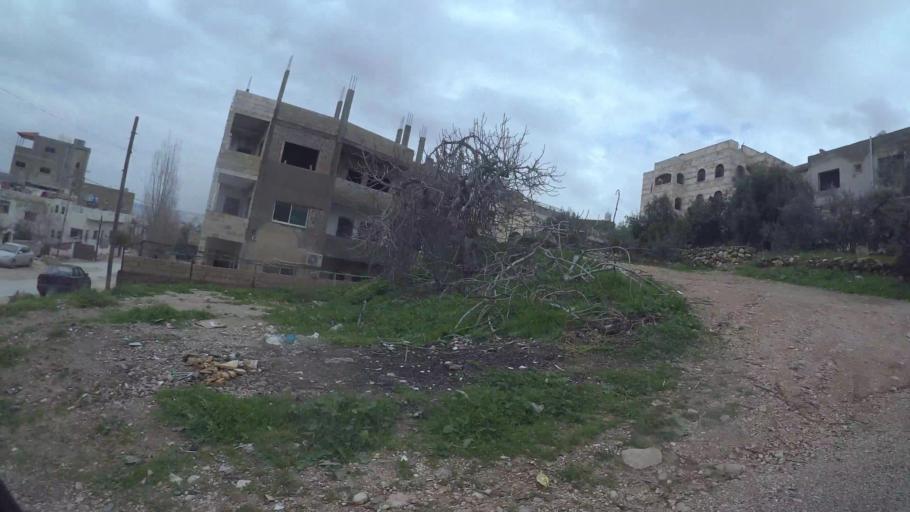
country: JO
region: Amman
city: Al Jubayhah
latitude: 32.0475
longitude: 35.8344
